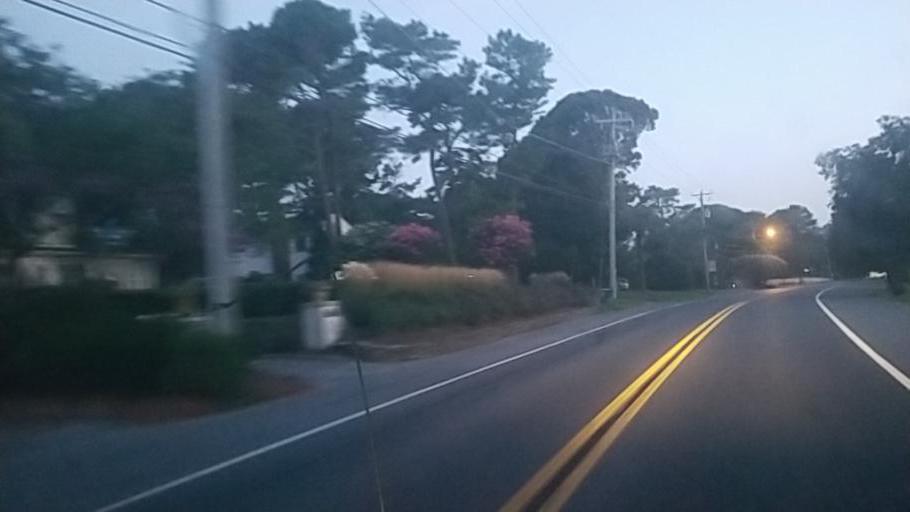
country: US
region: Delaware
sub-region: Sussex County
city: Rehoboth Beach
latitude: 38.7059
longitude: -75.0802
